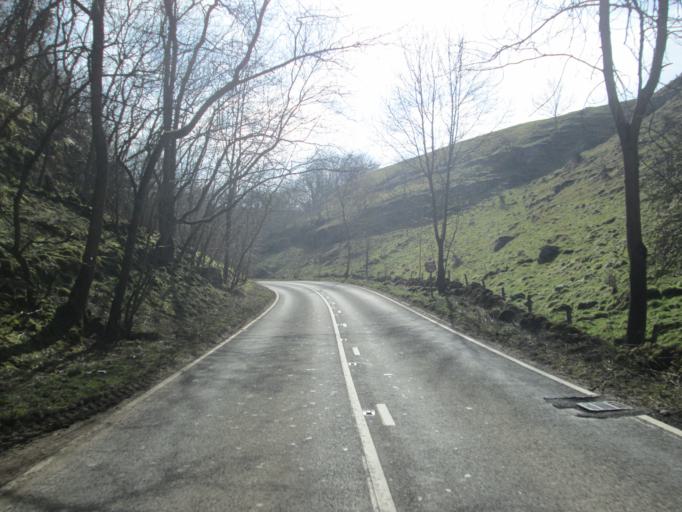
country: GB
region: England
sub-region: Derbyshire
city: Tideswell
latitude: 53.2511
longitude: -1.8032
